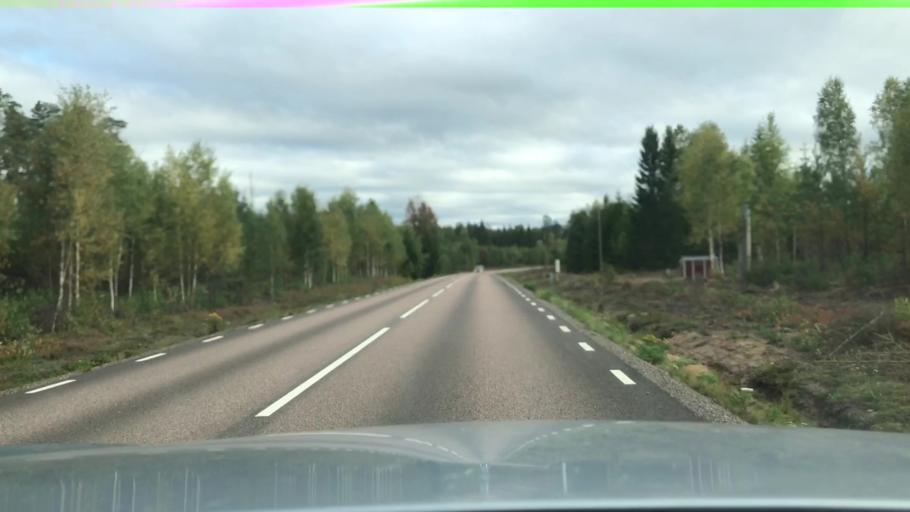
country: SE
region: Vaermland
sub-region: Forshaga Kommun
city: Forshaga
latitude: 59.5090
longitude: 13.4225
